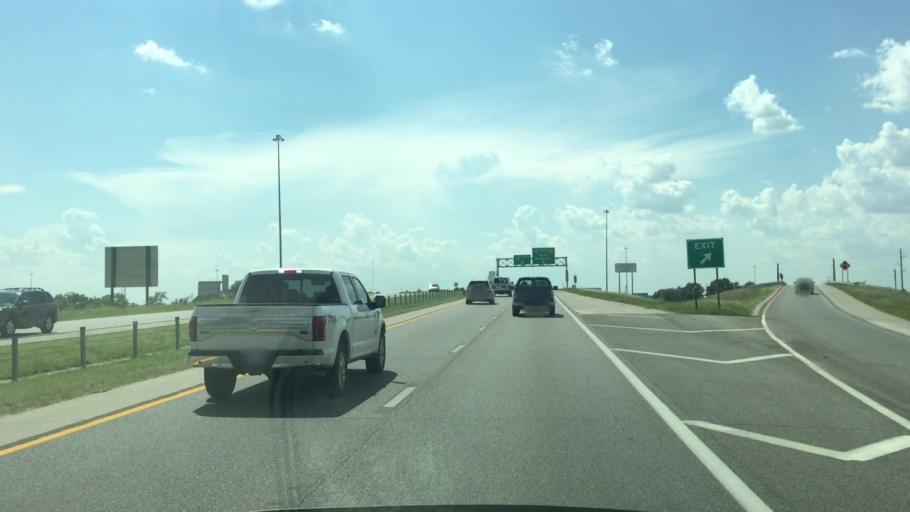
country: US
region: Kansas
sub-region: Sedgwick County
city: Bellaire
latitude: 37.7424
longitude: -97.3131
